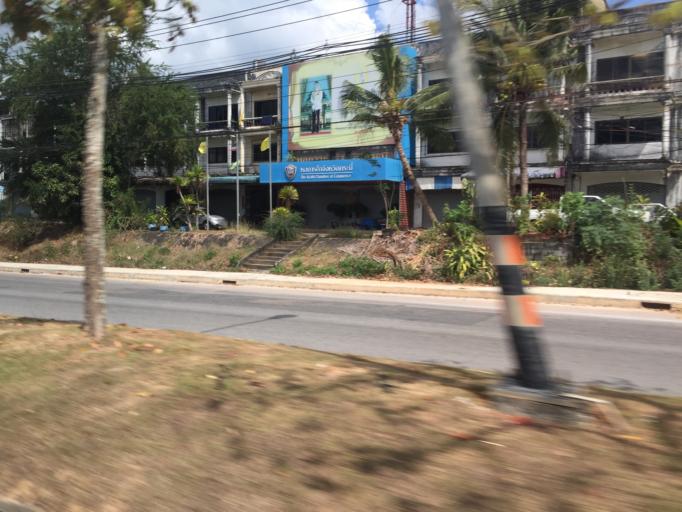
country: TH
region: Krabi
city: Krabi
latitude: 8.0955
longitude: 98.8885
